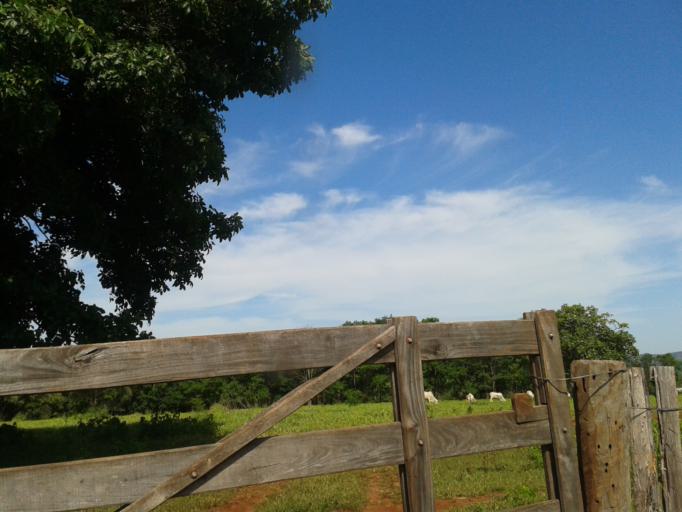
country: BR
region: Minas Gerais
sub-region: Santa Vitoria
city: Santa Vitoria
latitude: -19.0953
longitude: -50.0128
